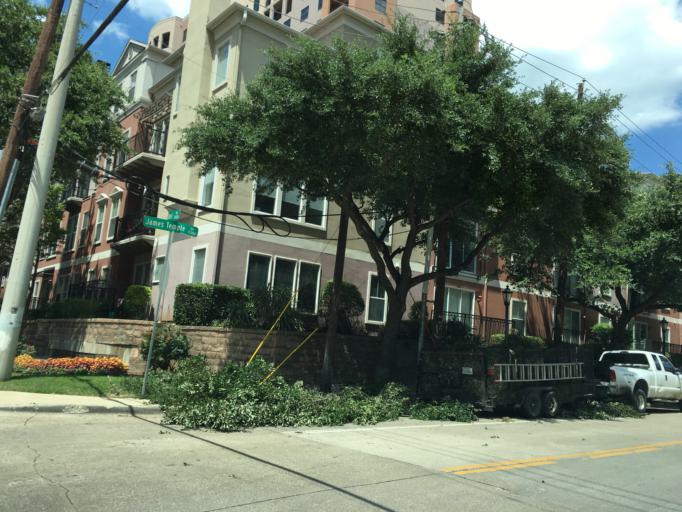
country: US
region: Texas
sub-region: Dallas County
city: Addison
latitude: 32.9291
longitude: -96.8180
